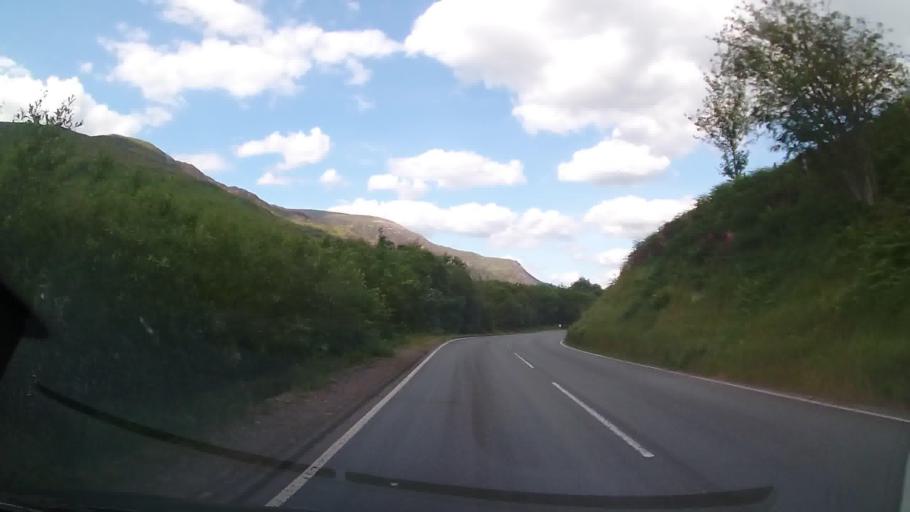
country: GB
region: Wales
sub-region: Gwynedd
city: Corris
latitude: 52.6709
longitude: -3.8979
